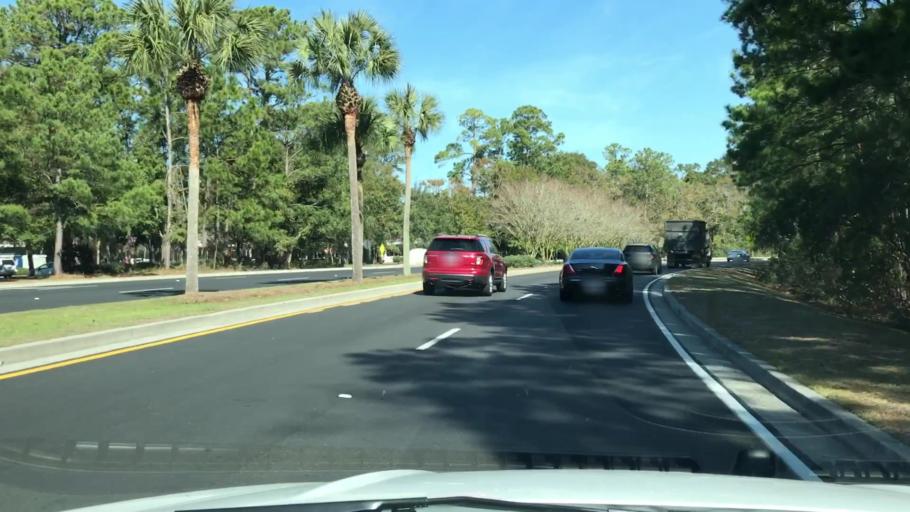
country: US
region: South Carolina
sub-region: Beaufort County
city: Hilton Head Island
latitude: 32.2195
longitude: -80.7122
